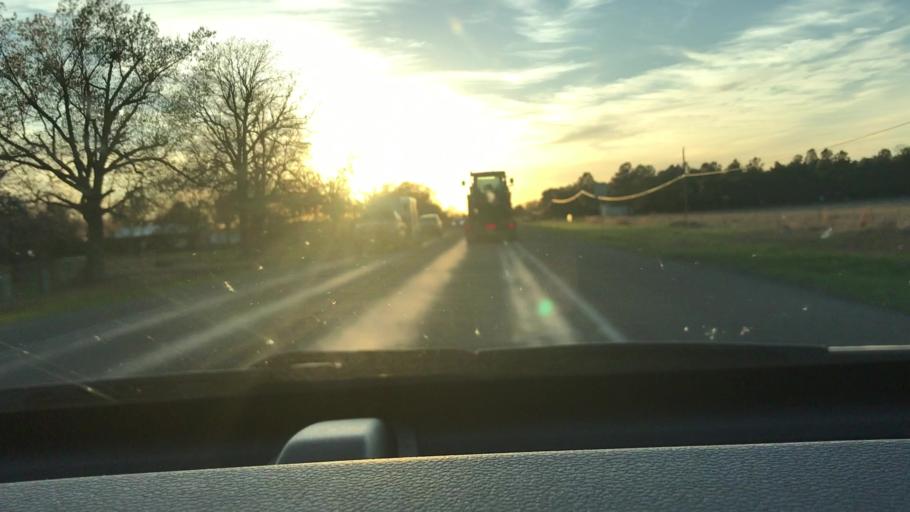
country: US
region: Texas
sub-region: Lamar County
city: Blossom
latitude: 33.6649
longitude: -95.3170
